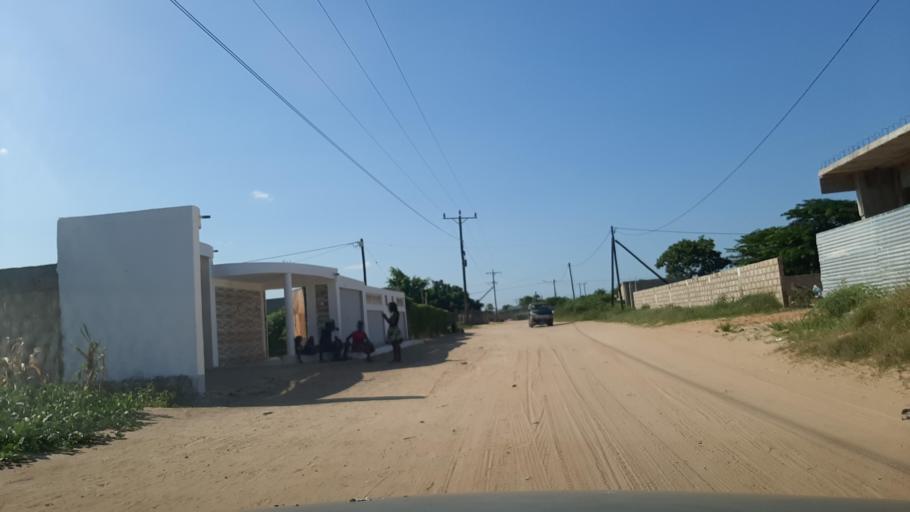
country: MZ
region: Maputo
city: Matola
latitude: -25.8114
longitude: 32.4917
